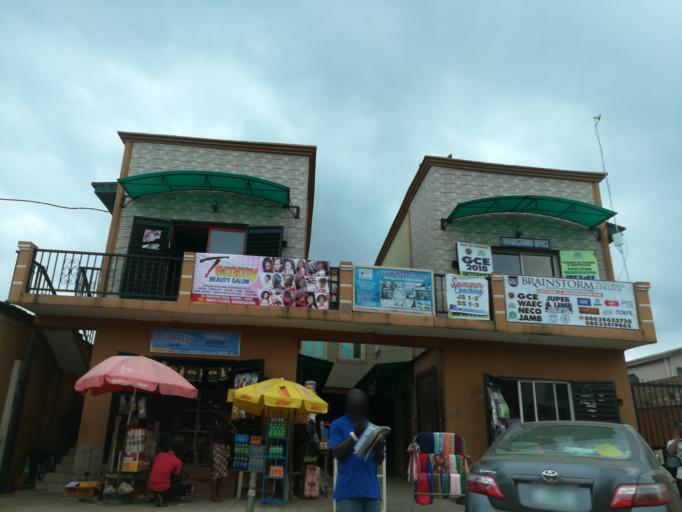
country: NG
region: Lagos
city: Oshodi
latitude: 6.5558
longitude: 3.3335
